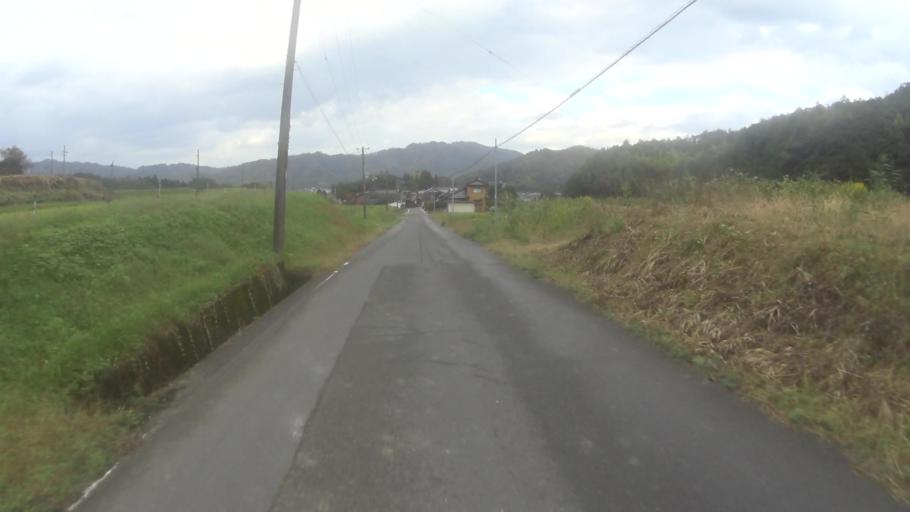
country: JP
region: Kyoto
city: Miyazu
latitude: 35.5186
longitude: 135.1257
